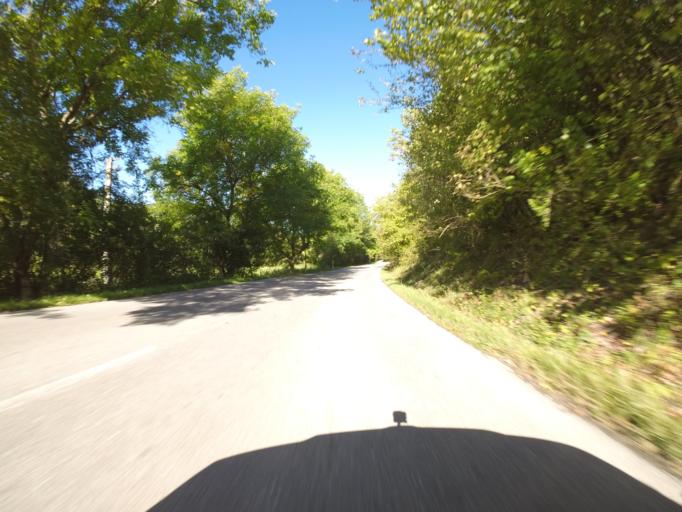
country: SK
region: Nitriansky
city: Ilava
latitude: 48.9682
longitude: 18.3553
